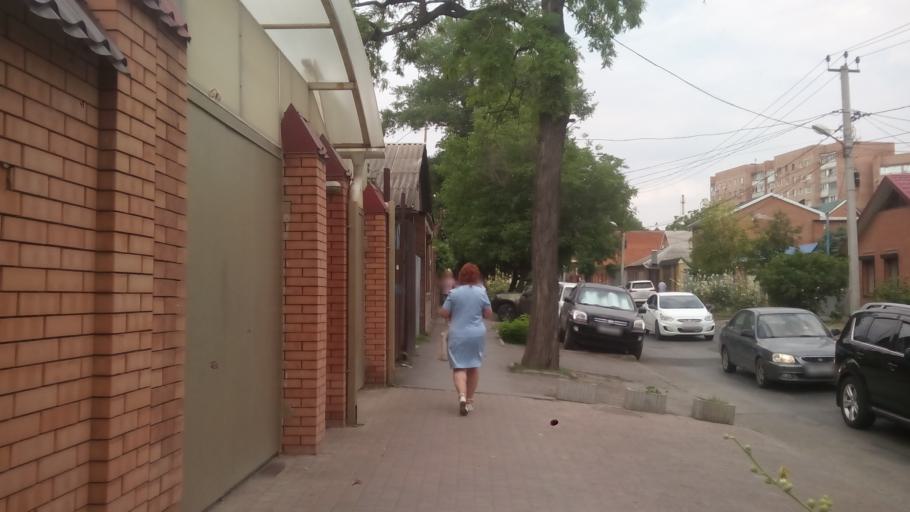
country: RU
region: Rostov
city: Rostov-na-Donu
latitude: 47.2126
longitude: 39.6739
